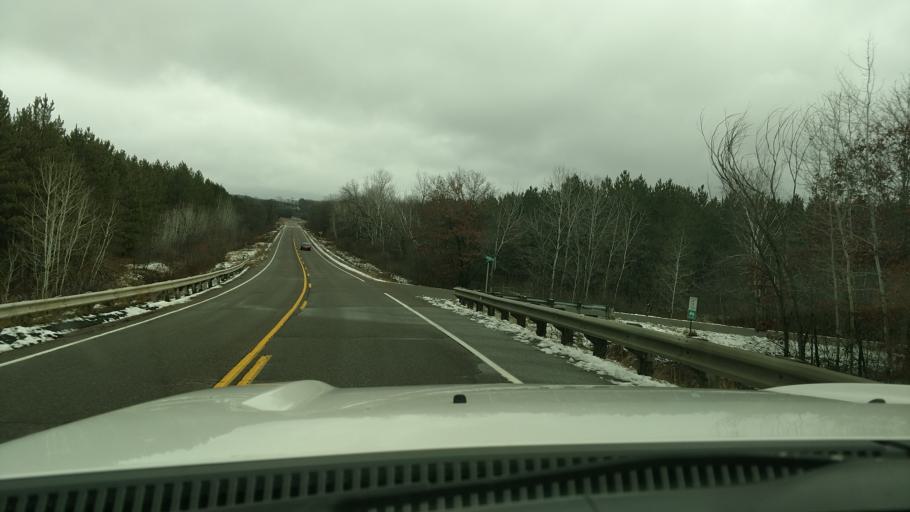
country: US
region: Wisconsin
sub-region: Dunn County
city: Boyceville
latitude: 45.1363
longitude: -91.9428
